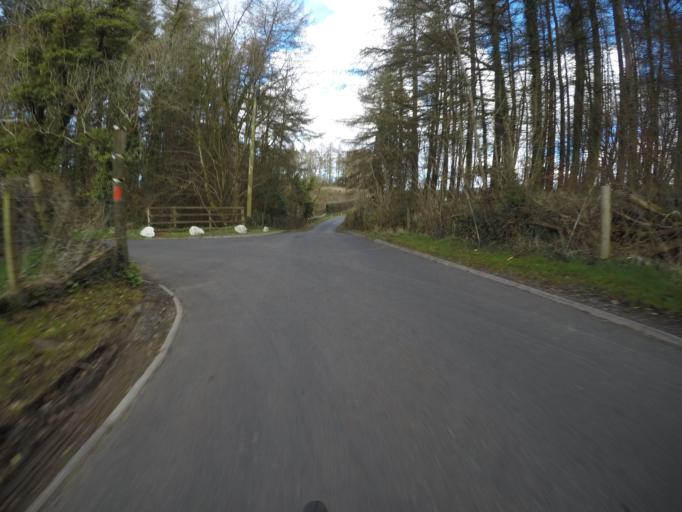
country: GB
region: Scotland
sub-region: North Ayrshire
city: Kilwinning
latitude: 55.6916
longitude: -4.6735
